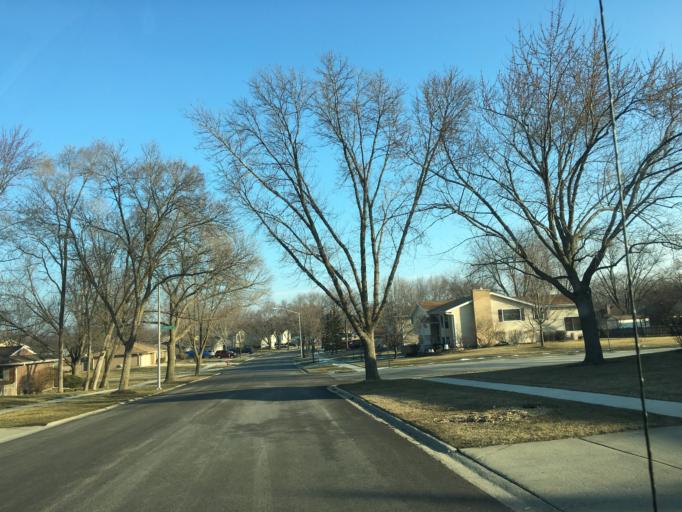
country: US
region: Illinois
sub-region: Cook County
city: Schaumburg
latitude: 42.0198
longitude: -88.0960
